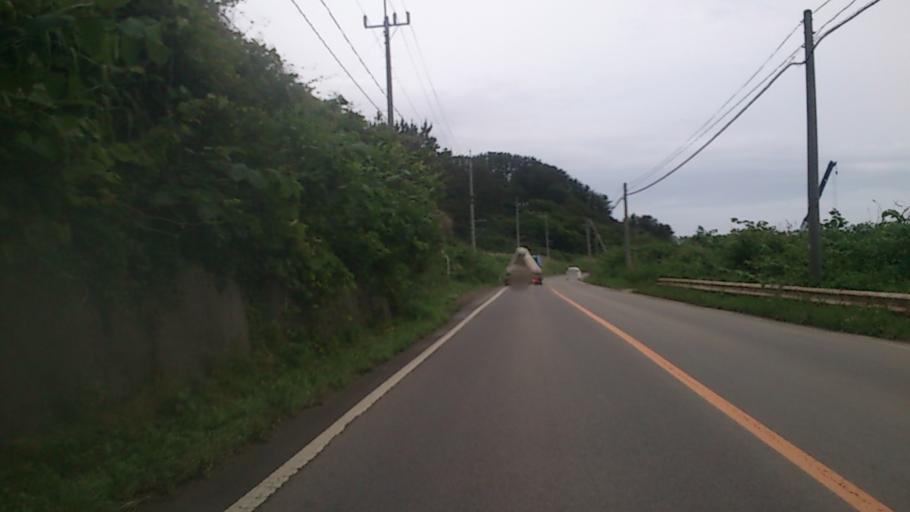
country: JP
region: Akita
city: Noshiromachi
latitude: 40.5090
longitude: 139.9507
